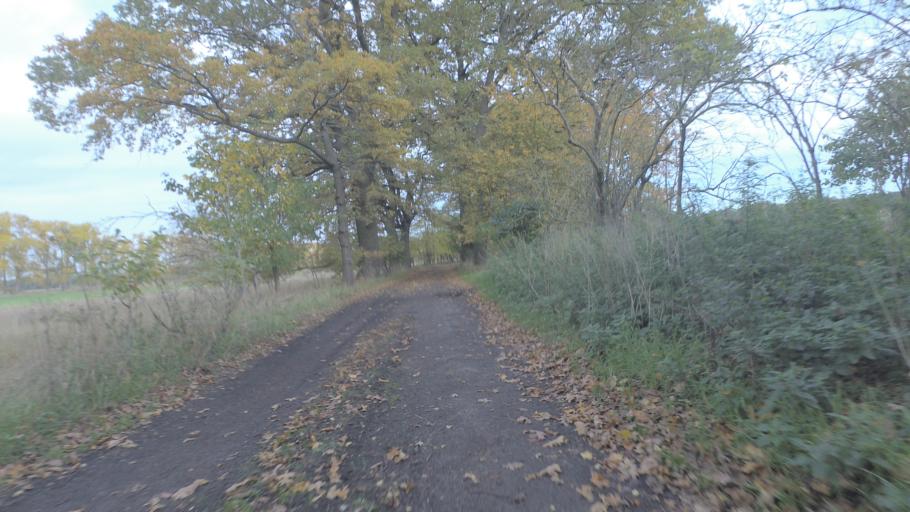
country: DE
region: Brandenburg
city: Ludwigsfelde
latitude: 52.2557
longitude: 13.2817
